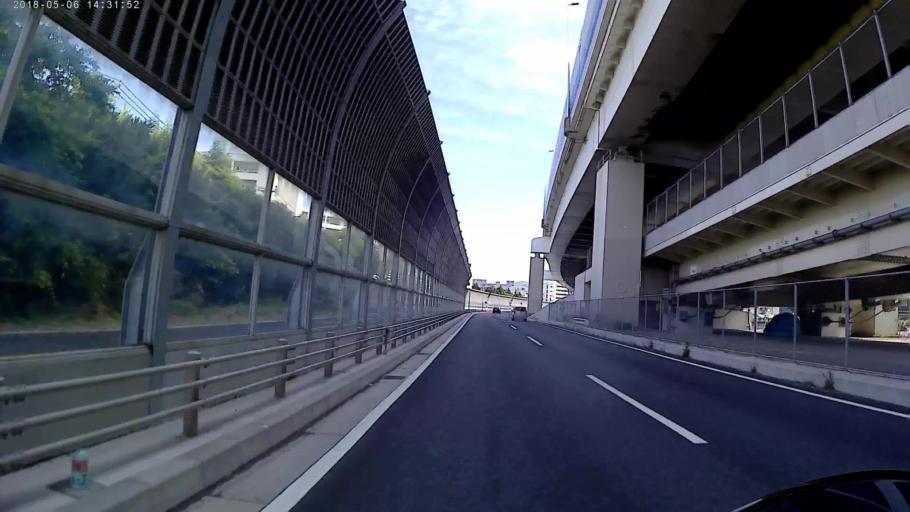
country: JP
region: Kanagawa
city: Yokohama
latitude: 35.4301
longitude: 139.6713
